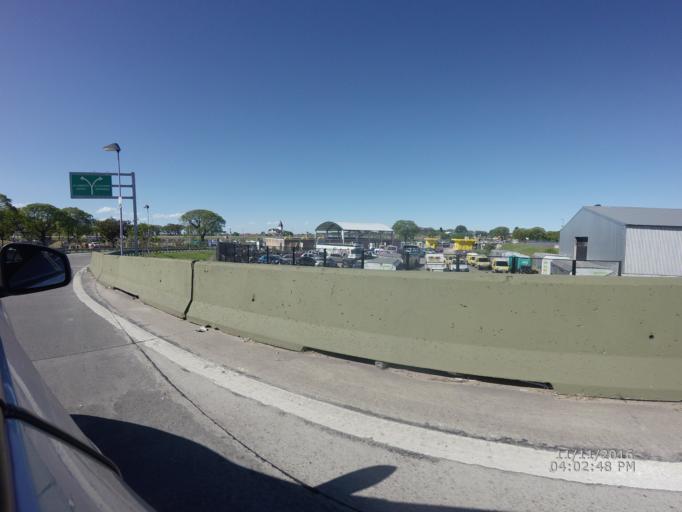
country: AR
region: Buenos Aires F.D.
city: Retiro
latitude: -34.5682
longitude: -58.4056
